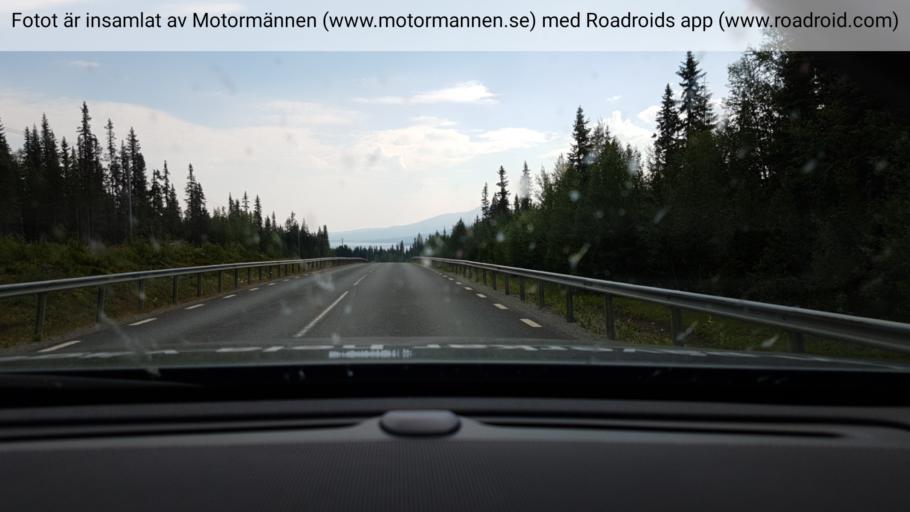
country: SE
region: Vaesterbotten
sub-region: Vilhelmina Kommun
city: Sjoberg
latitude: 65.5015
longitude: 15.6774
